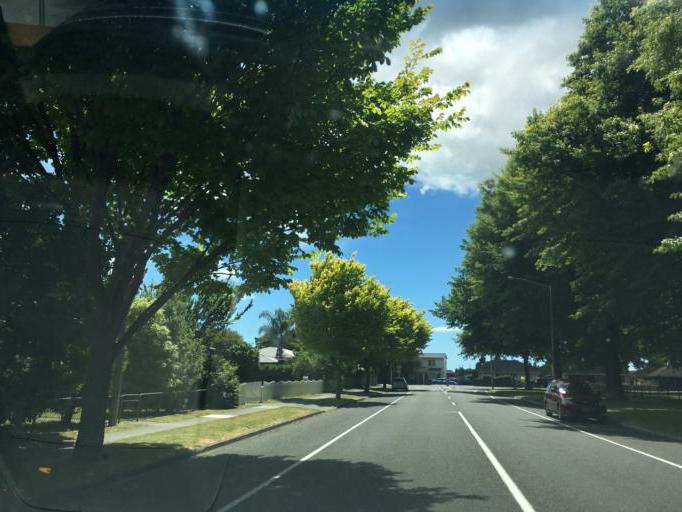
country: NZ
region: Hawke's Bay
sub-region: Hastings District
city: Hastings
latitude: -39.6427
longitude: 176.8621
